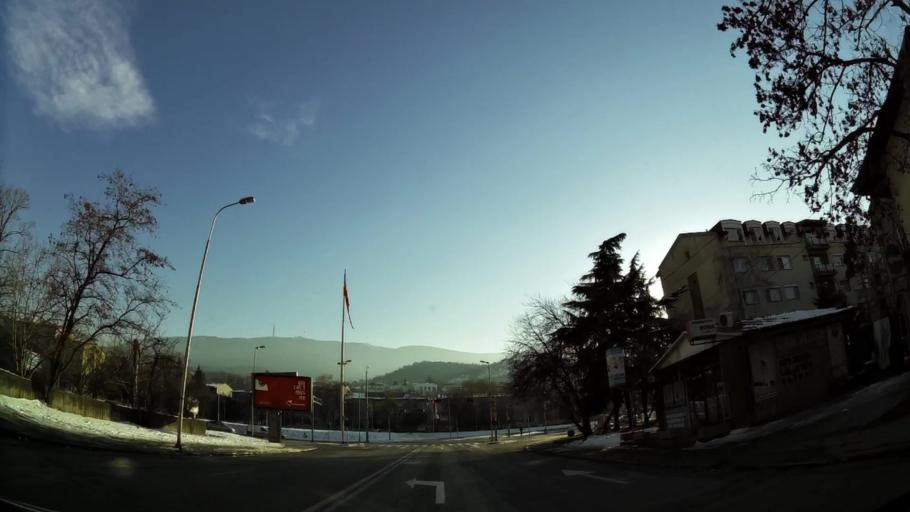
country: MK
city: Krushopek
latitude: 41.9990
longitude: 21.3891
